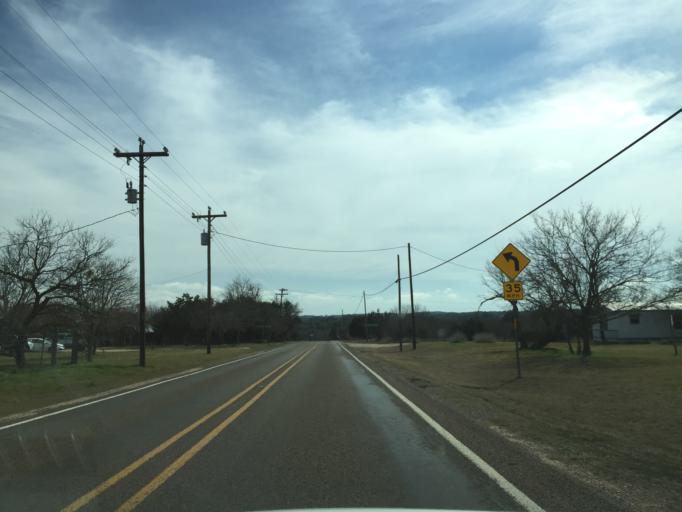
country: US
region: Texas
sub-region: Gillespie County
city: Fredericksburg
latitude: 30.3998
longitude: -98.7015
